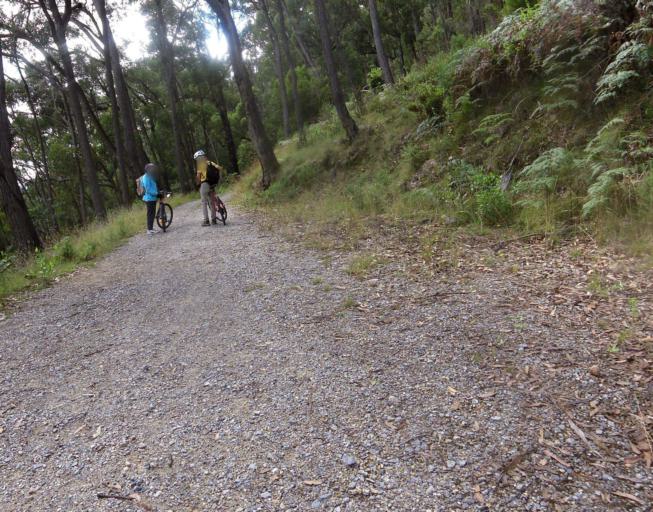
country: AU
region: Victoria
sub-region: Yarra Ranges
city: Montrose
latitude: -37.8243
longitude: 145.3485
